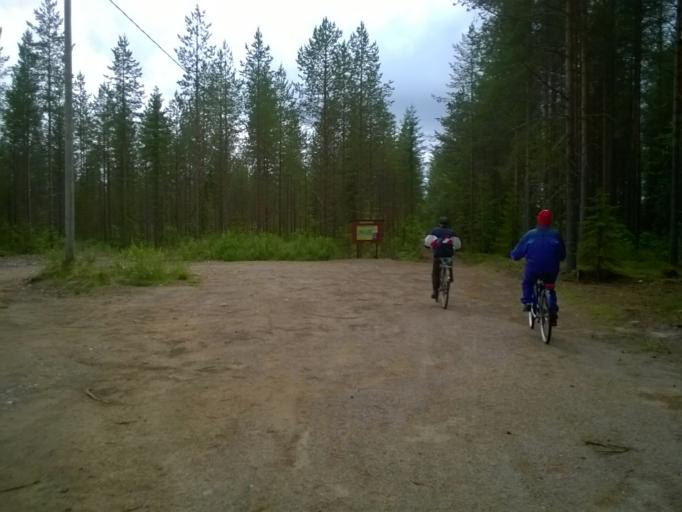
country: FI
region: Kainuu
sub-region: Kehys-Kainuu
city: Kuhmo
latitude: 64.1299
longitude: 29.4031
